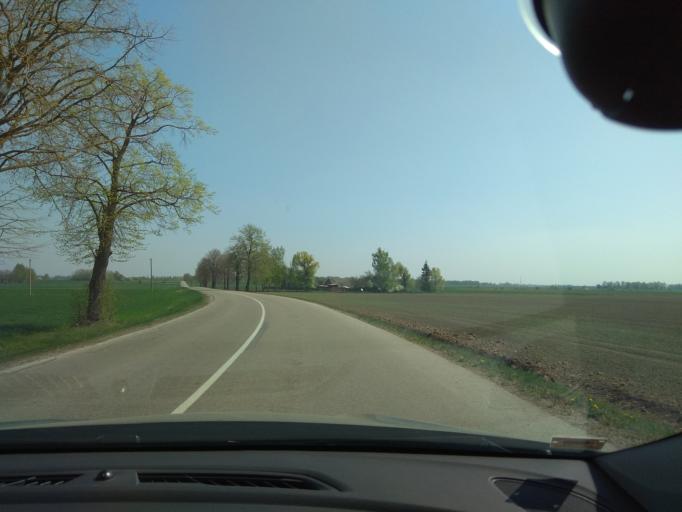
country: LT
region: Panevezys
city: Pasvalys
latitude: 55.9437
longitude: 24.2141
